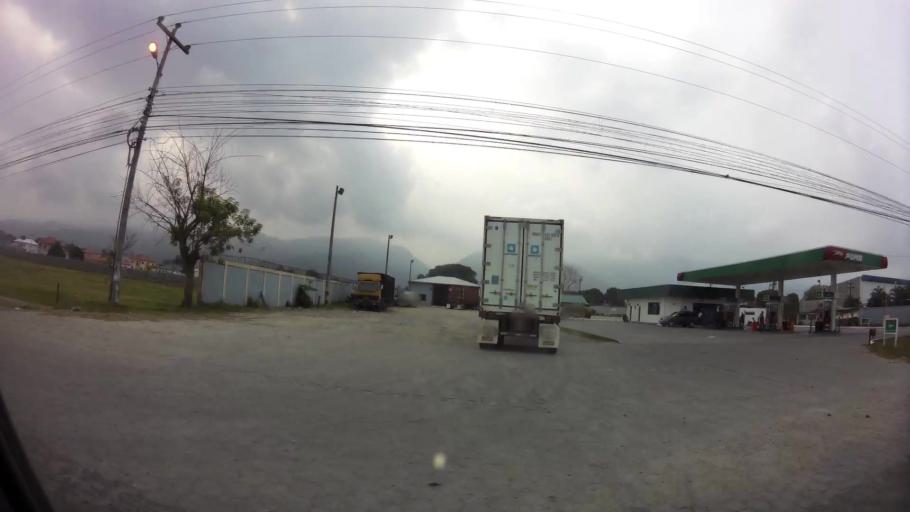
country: HN
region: Yoro
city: El Progreso
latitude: 15.4320
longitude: -87.7955
